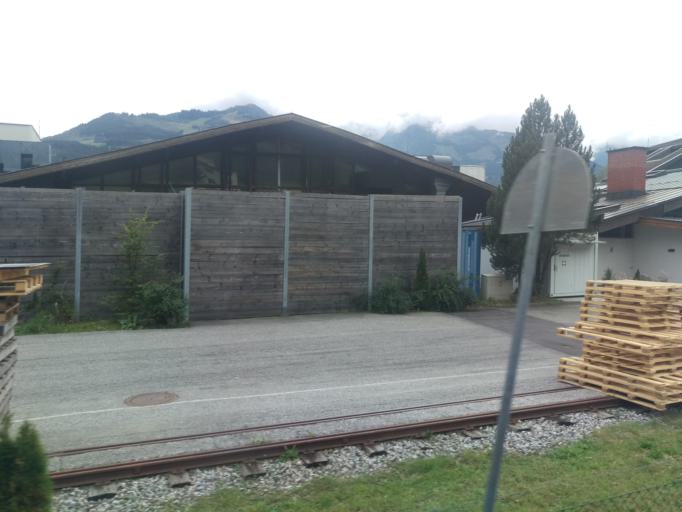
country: AT
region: Salzburg
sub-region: Politischer Bezirk Zell am See
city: Piesendorf
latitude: 47.2911
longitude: 12.7285
